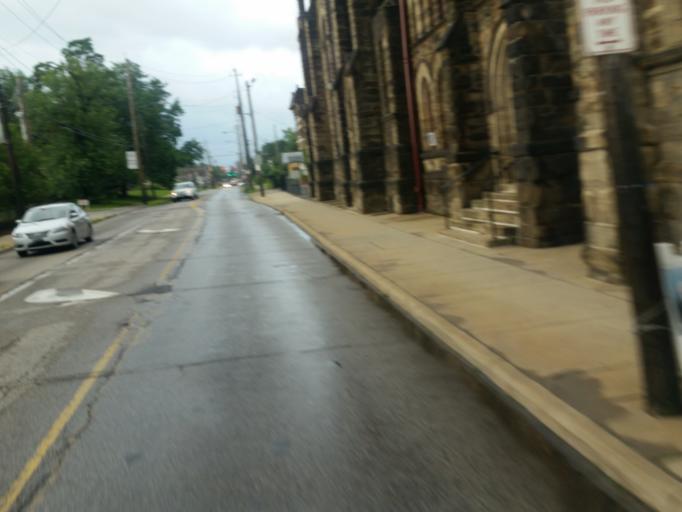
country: US
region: Ohio
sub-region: Cuyahoga County
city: Bratenahl
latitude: 41.5034
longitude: -81.6336
